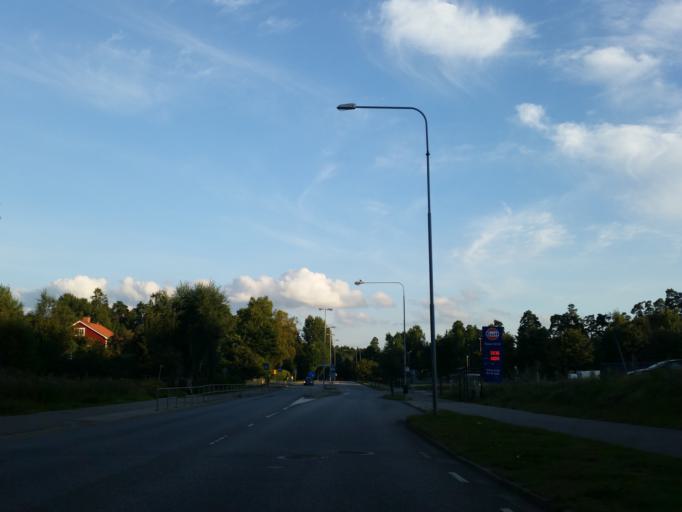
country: SE
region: Stockholm
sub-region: Sodertalje Kommun
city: Soedertaelje
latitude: 59.2067
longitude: 17.6000
